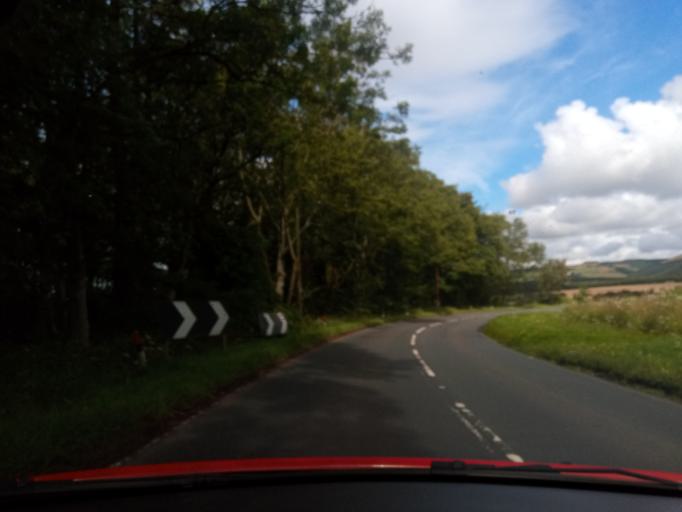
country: GB
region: Scotland
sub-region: The Scottish Borders
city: Lauder
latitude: 55.7239
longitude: -2.7271
